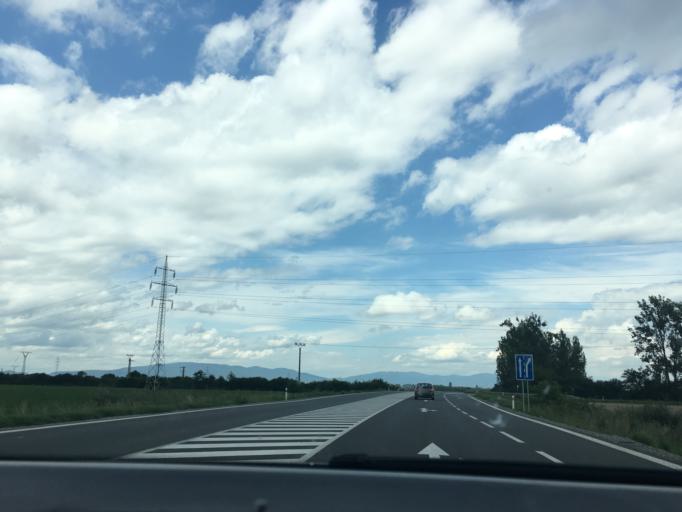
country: SK
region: Kosicky
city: Trebisov
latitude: 48.6019
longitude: 21.7118
